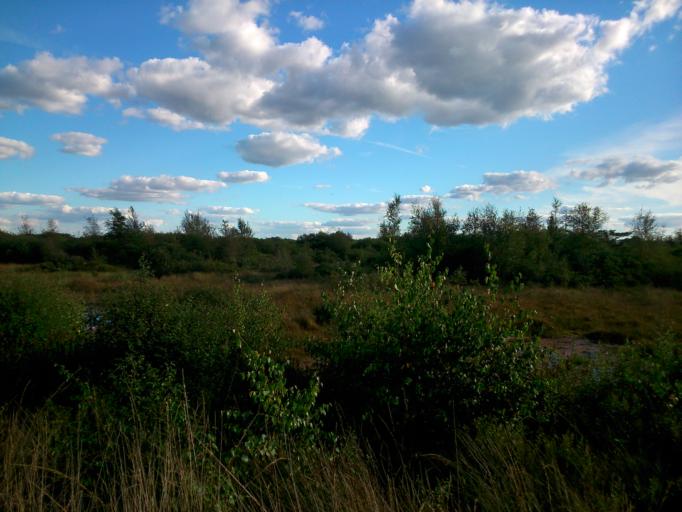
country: DK
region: Central Jutland
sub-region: Ringkobing-Skjern Kommune
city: Tarm
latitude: 55.9455
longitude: 8.5895
